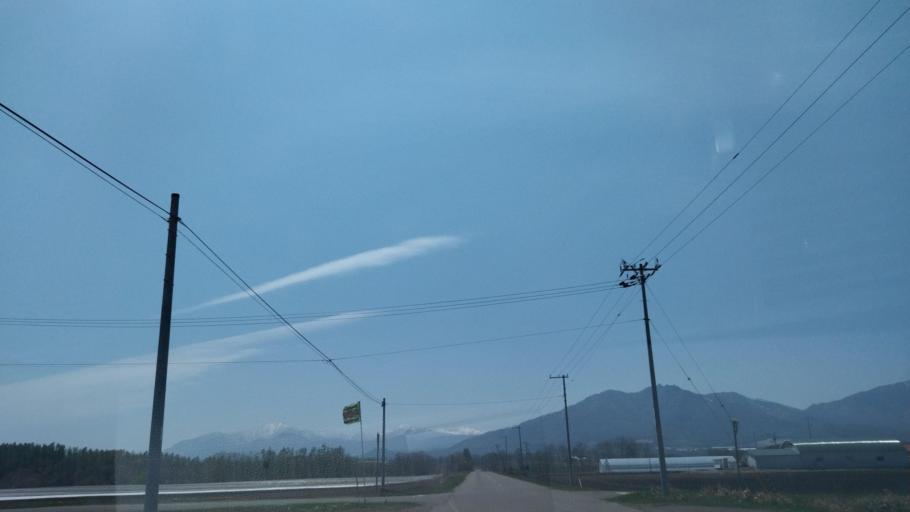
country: JP
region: Hokkaido
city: Obihiro
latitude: 42.9009
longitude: 142.9828
